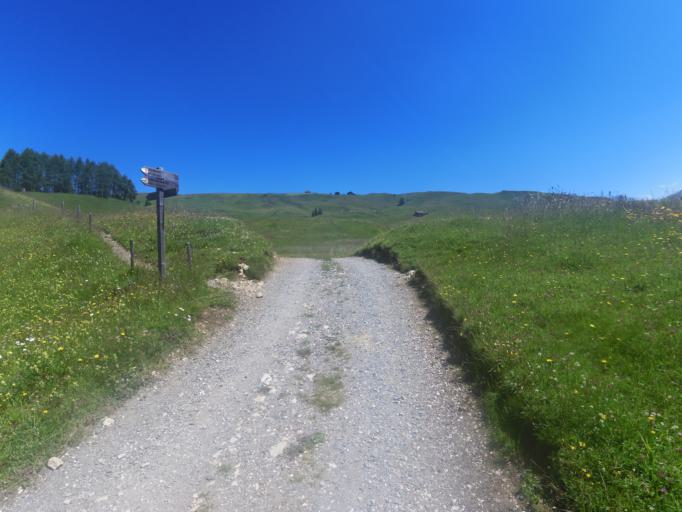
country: IT
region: Trentino-Alto Adige
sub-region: Bolzano
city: Siusi
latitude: 46.5210
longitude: 11.6049
